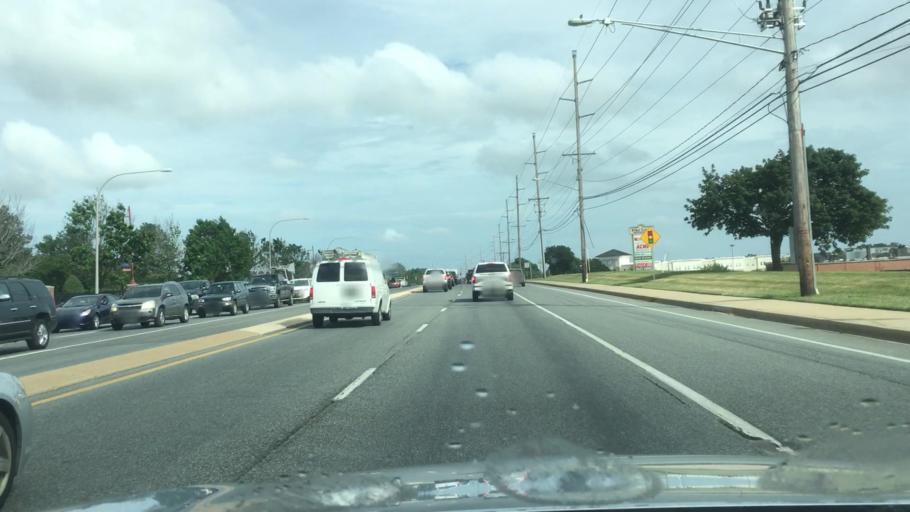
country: US
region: Delaware
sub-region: New Castle County
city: Pike Creek Valley
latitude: 39.7415
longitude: -75.6919
